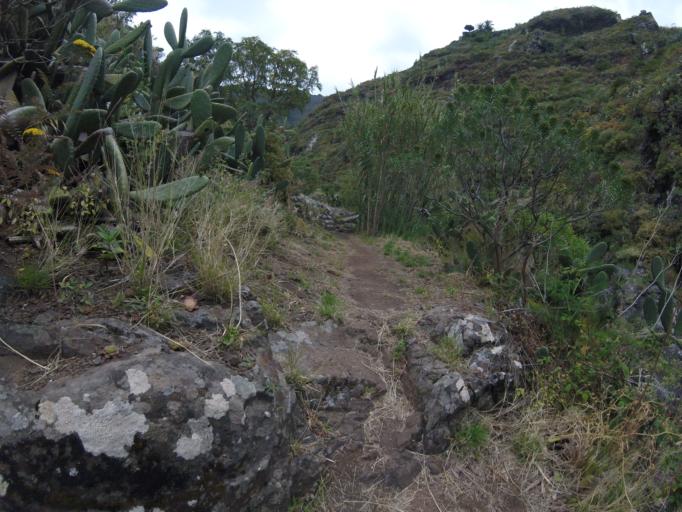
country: ES
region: Canary Islands
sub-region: Provincia de Santa Cruz de Tenerife
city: Tegueste
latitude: 28.5490
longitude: -16.2933
